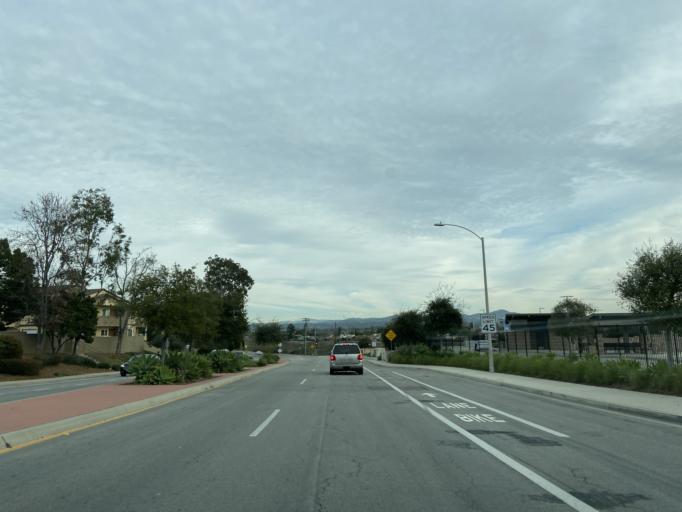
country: US
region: California
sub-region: San Diego County
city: Camp Pendleton North
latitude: 33.2547
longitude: -117.2984
